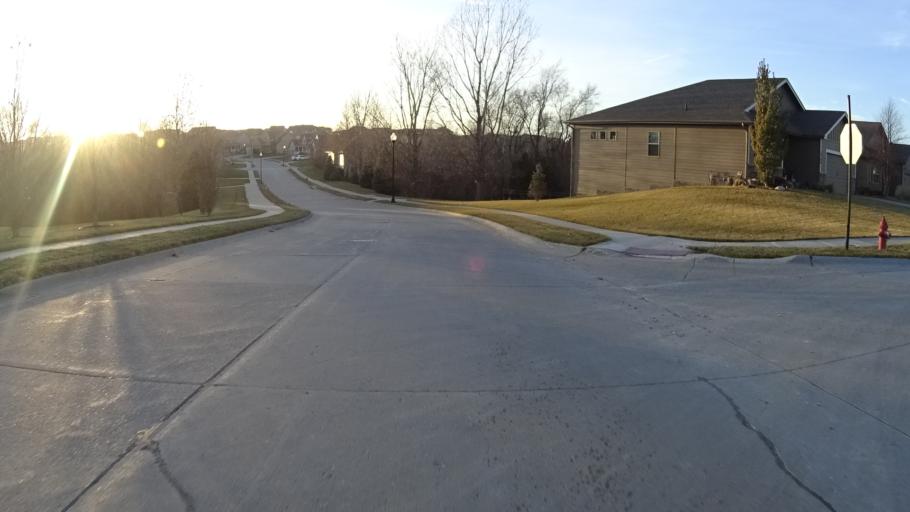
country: US
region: Nebraska
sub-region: Sarpy County
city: Papillion
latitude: 41.1307
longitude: -96.0635
